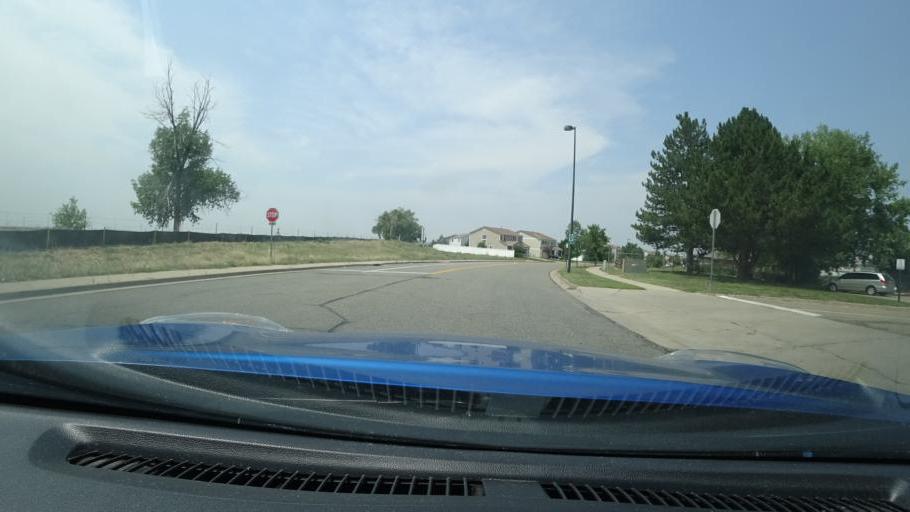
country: US
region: Colorado
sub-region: Adams County
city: Aurora
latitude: 39.7717
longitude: -104.7656
